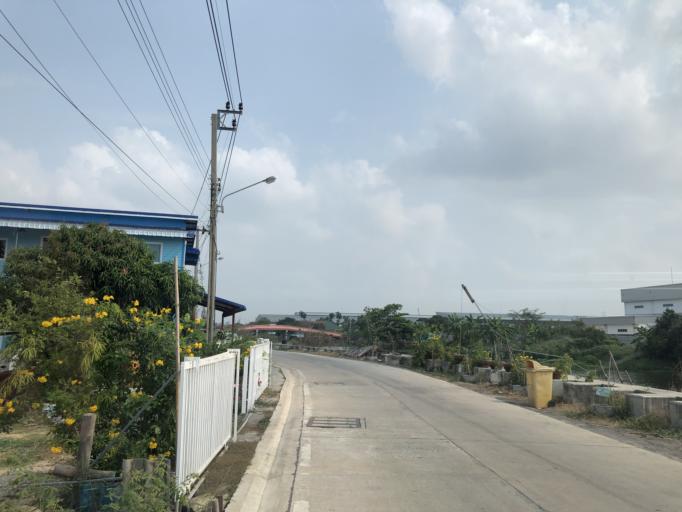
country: TH
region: Samut Prakan
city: Bang Bo District
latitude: 13.5835
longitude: 100.7476
